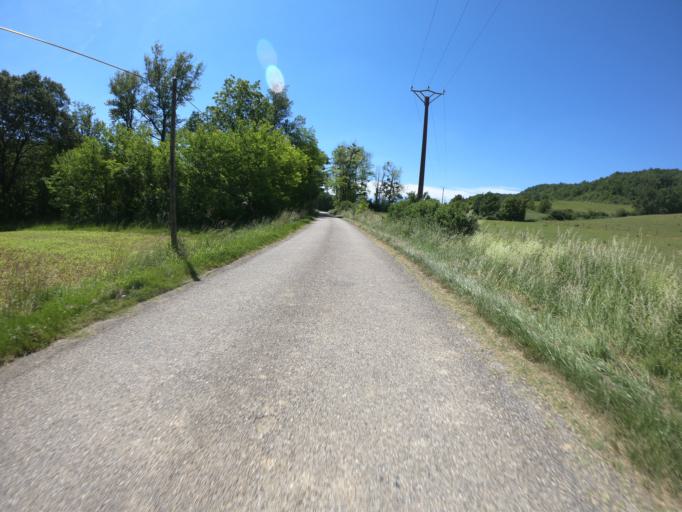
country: FR
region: Midi-Pyrenees
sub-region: Departement de l'Ariege
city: Mirepoix
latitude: 43.1007
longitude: 1.7763
